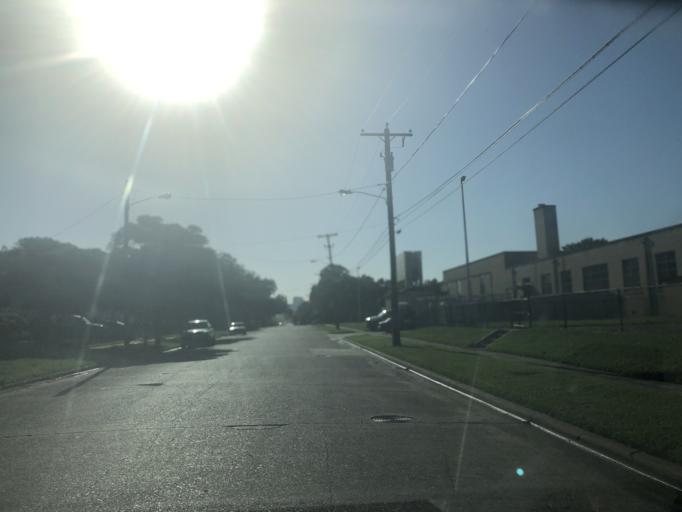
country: US
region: Texas
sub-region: Dallas County
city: Dallas
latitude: 32.7887
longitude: -96.8535
